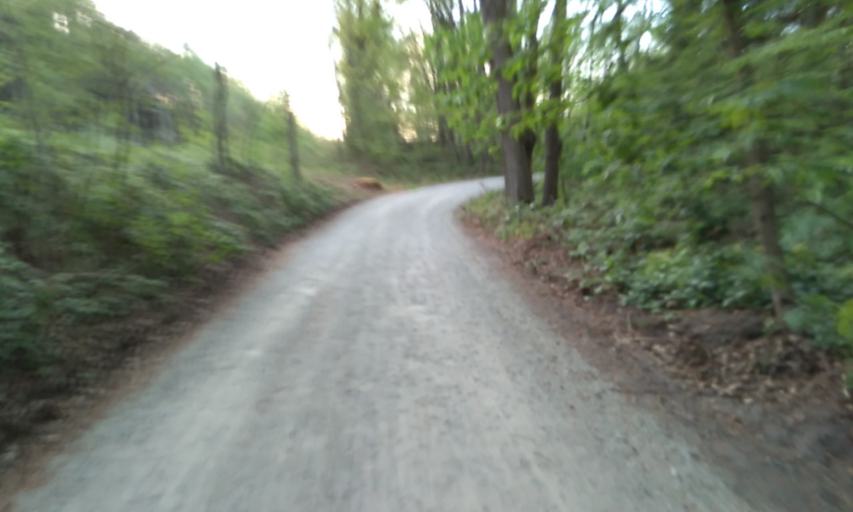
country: DE
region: Lower Saxony
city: Nottensdorf
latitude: 53.4914
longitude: 9.6150
